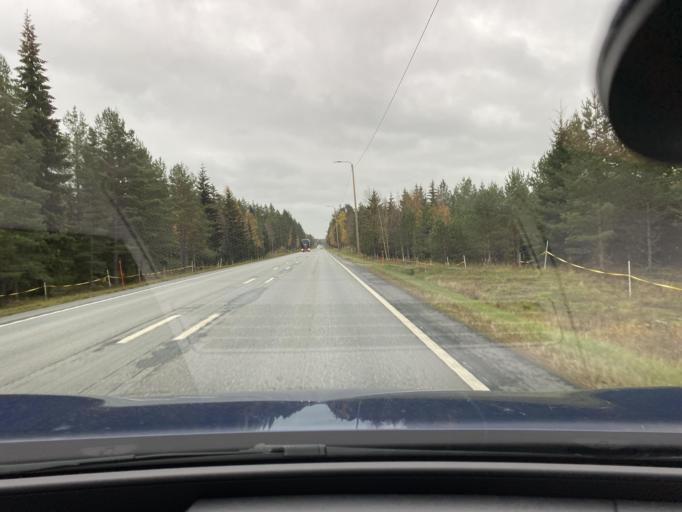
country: FI
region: Varsinais-Suomi
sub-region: Vakka-Suomi
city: Laitila
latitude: 60.9520
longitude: 21.5979
